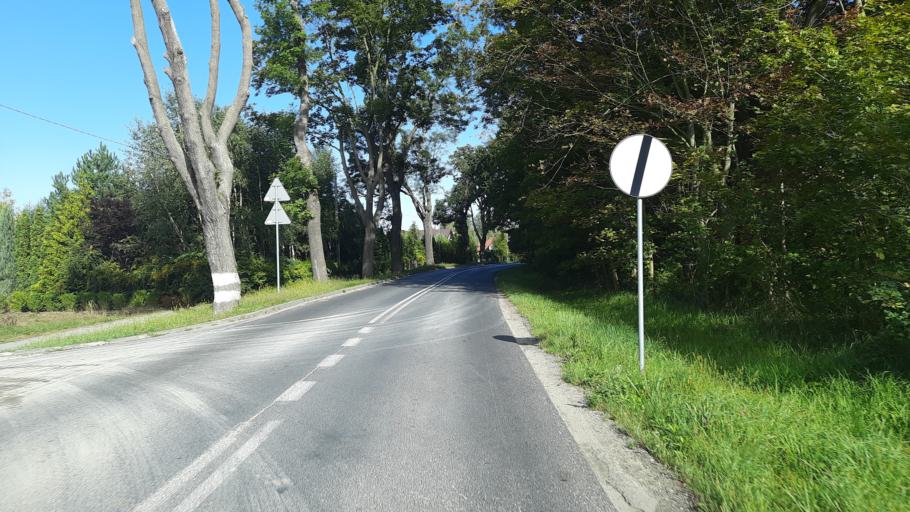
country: PL
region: Lower Silesian Voivodeship
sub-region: Powiat wroclawski
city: Dlugoleka
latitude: 51.1856
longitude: 17.1862
